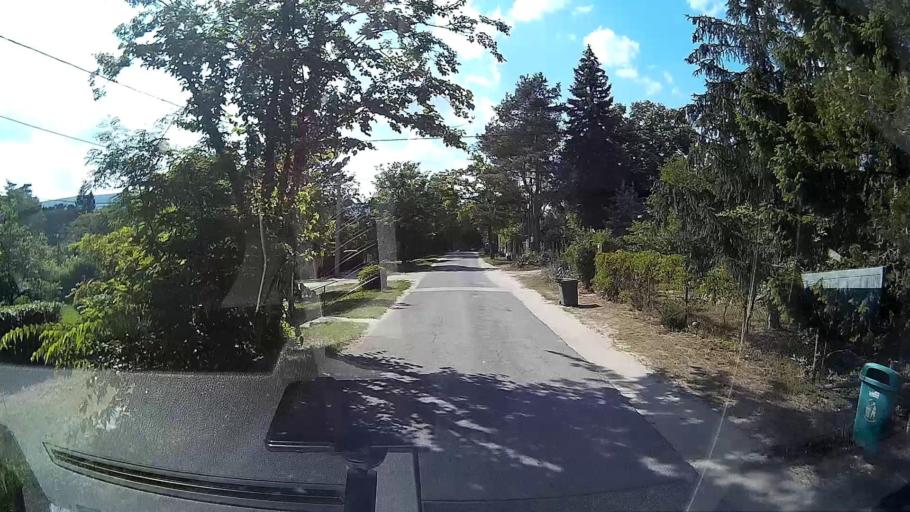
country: HU
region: Pest
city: Leanyfalu
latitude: 47.7144
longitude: 19.1128
